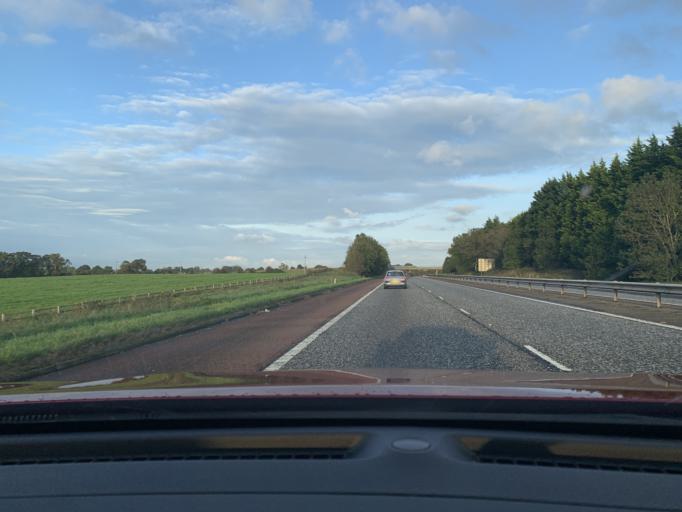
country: GB
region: Northern Ireland
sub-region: Craigavon District
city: Craigavon
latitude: 54.4884
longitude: -6.3424
